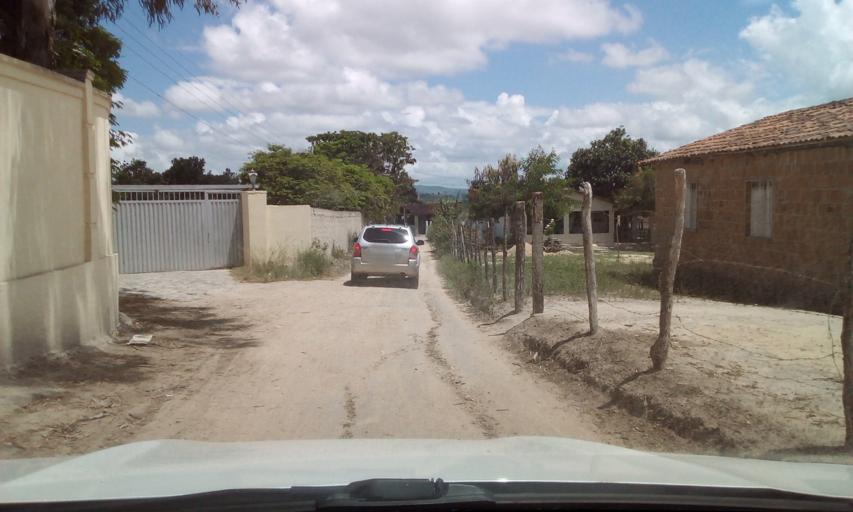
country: BR
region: Pernambuco
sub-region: Cha Grande
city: Cha Grande
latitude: -8.1935
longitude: -35.4960
